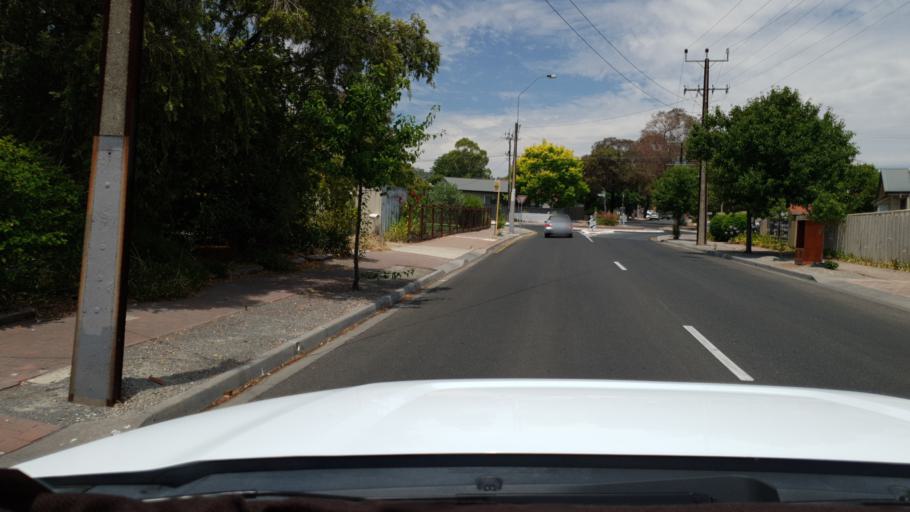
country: AU
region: South Australia
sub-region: Marion
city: Clovelly Park
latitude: -35.0009
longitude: 138.5833
